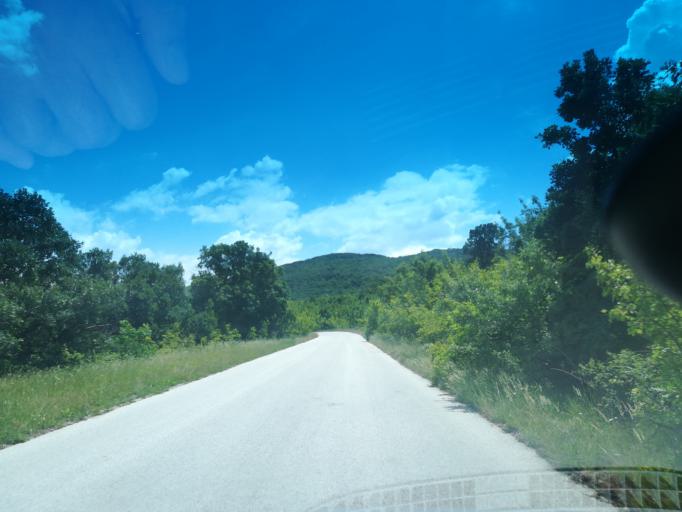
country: BG
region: Khaskovo
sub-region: Obshtina Mineralni Bani
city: Mineralni Bani
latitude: 41.9805
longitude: 25.2473
